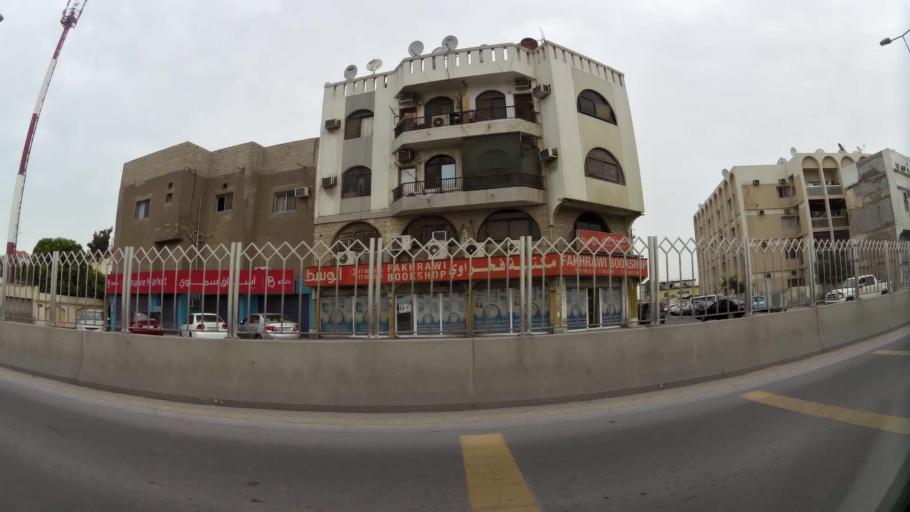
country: BH
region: Manama
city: Jidd Hafs
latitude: 26.2168
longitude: 50.5325
